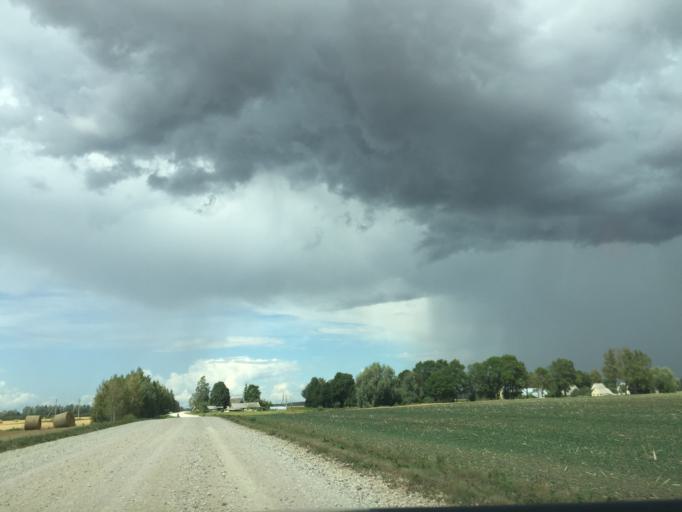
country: LT
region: Siauliu apskritis
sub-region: Joniskis
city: Joniskis
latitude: 56.2825
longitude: 23.7245
